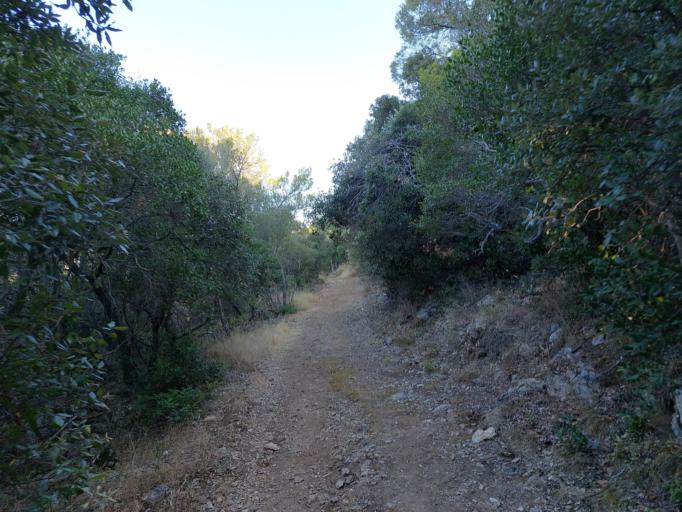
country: HR
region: Dubrovacko-Neretvanska
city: Smokvica
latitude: 42.7578
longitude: 16.8091
